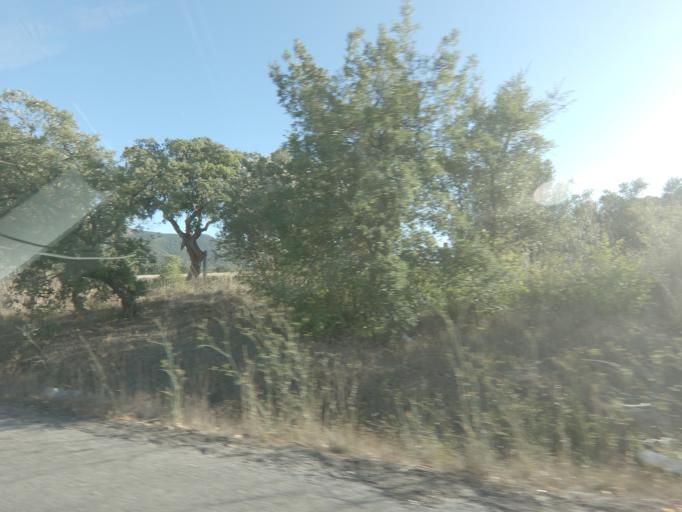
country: PT
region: Setubal
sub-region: Palmela
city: Quinta do Anjo
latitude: 38.5201
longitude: -8.9828
